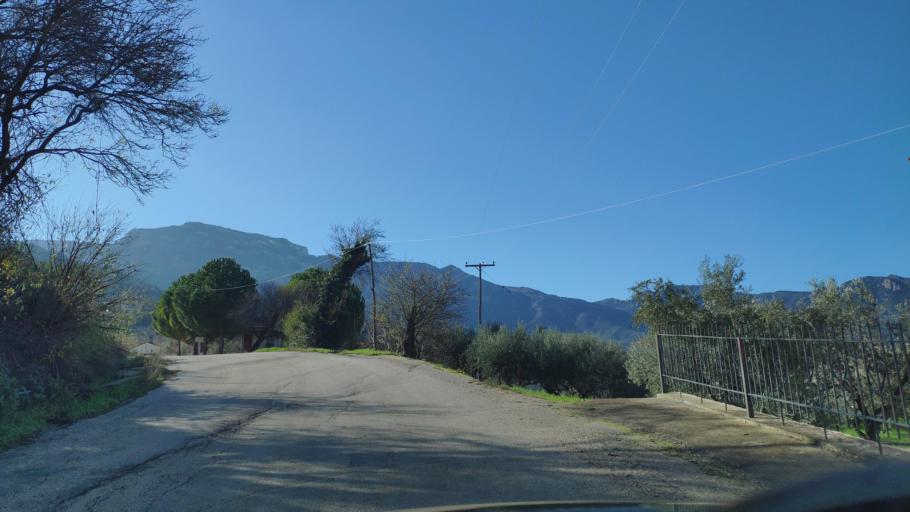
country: GR
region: West Greece
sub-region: Nomos Achaias
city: Aiyira
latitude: 38.0916
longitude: 22.4385
